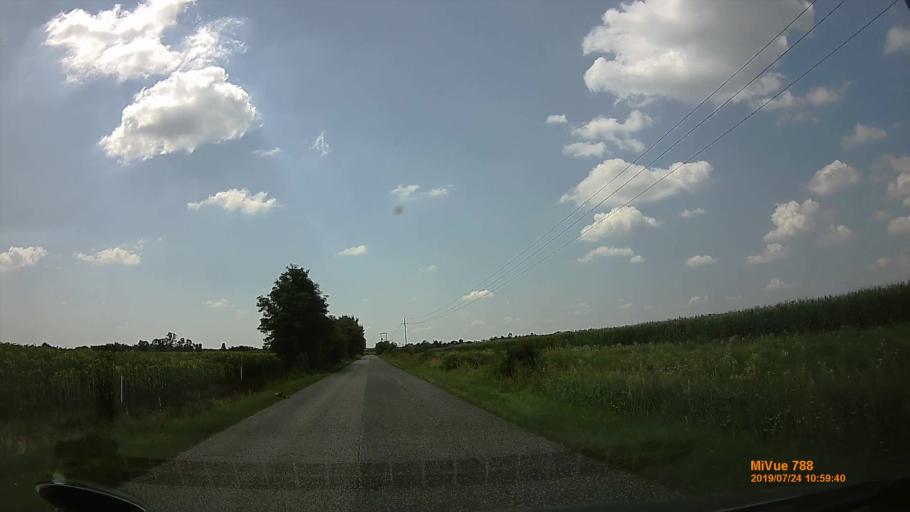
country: HU
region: Szabolcs-Szatmar-Bereg
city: Tarpa
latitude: 48.1633
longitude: 22.5161
